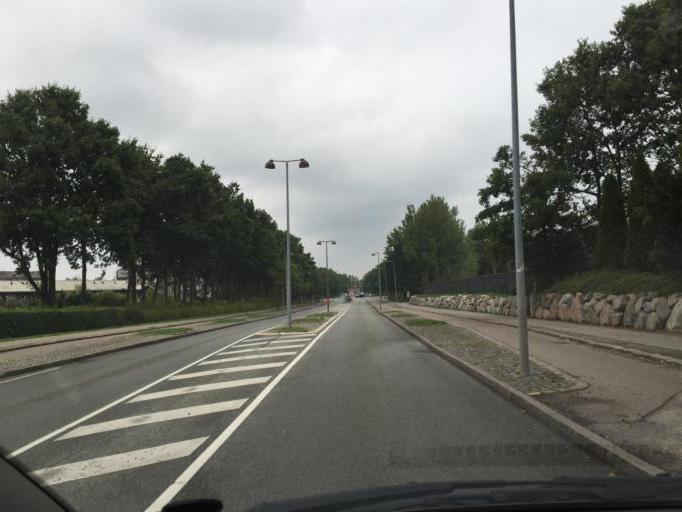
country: DK
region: Capital Region
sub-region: Herlev Kommune
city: Herlev
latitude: 55.7387
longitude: 12.4309
